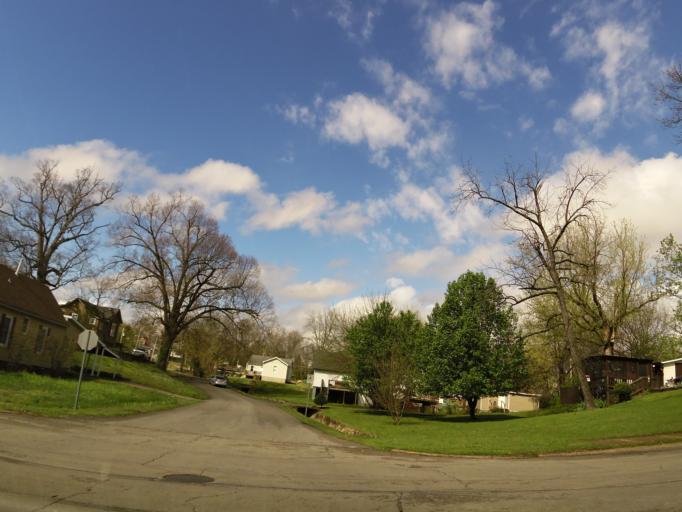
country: US
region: Missouri
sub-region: Butler County
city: Poplar Bluff
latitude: 36.7655
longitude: -90.3994
